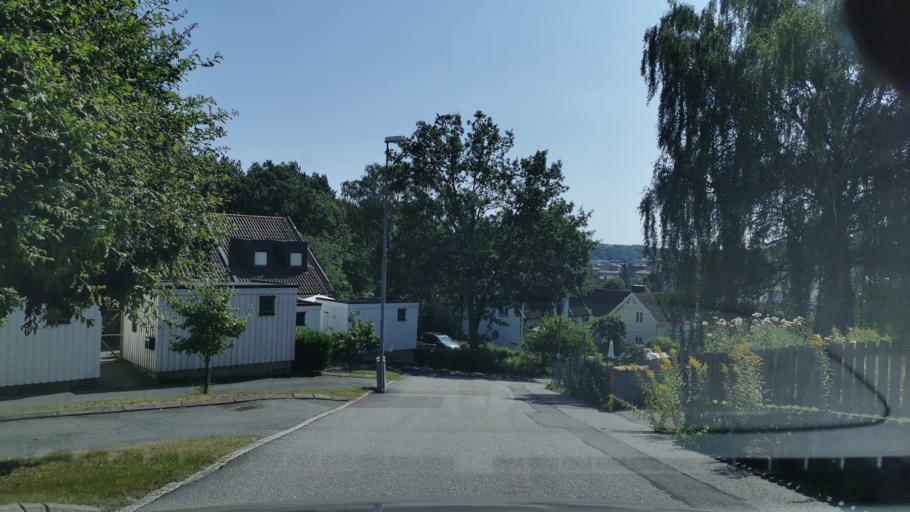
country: SE
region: Vaestra Goetaland
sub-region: Molndal
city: Moelndal
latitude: 57.6778
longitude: 11.9987
